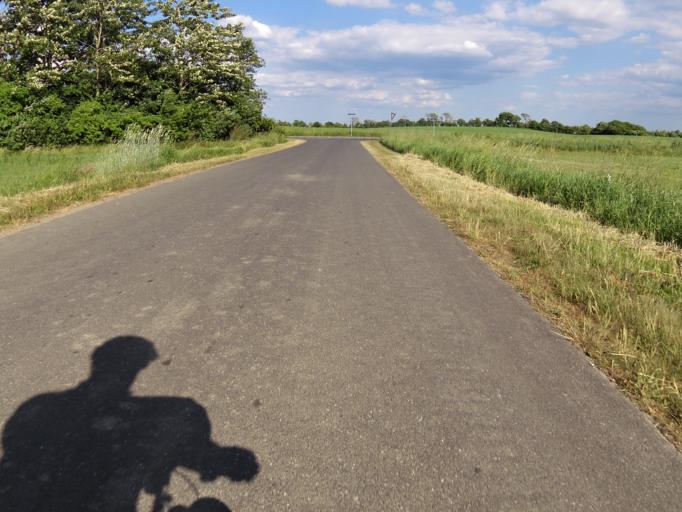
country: DK
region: Central Jutland
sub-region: Holstebro Kommune
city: Vinderup
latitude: 56.4576
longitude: 8.8474
